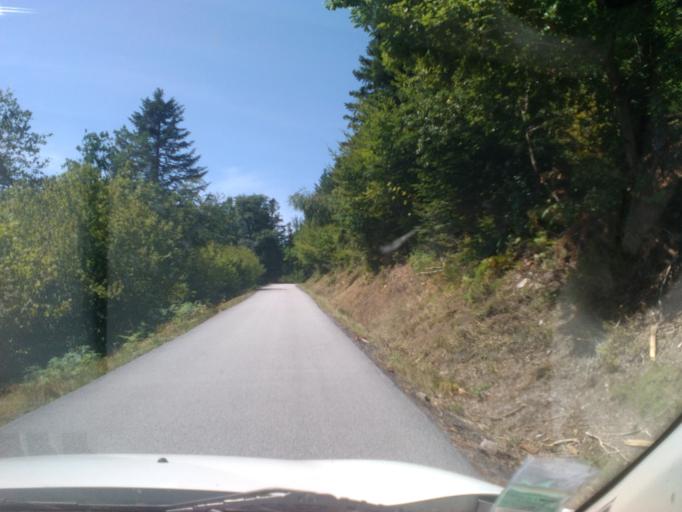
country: FR
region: Lorraine
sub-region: Departement des Vosges
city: Le Tholy
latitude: 48.0311
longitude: 6.7692
